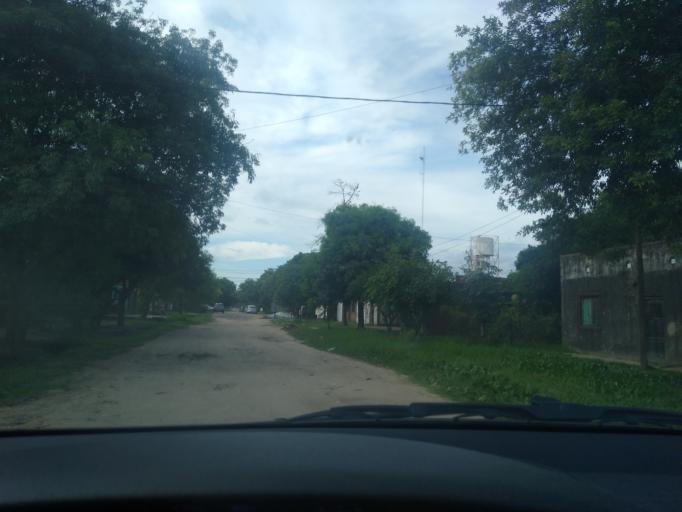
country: AR
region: Chaco
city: Resistencia
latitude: -27.4856
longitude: -58.9712
